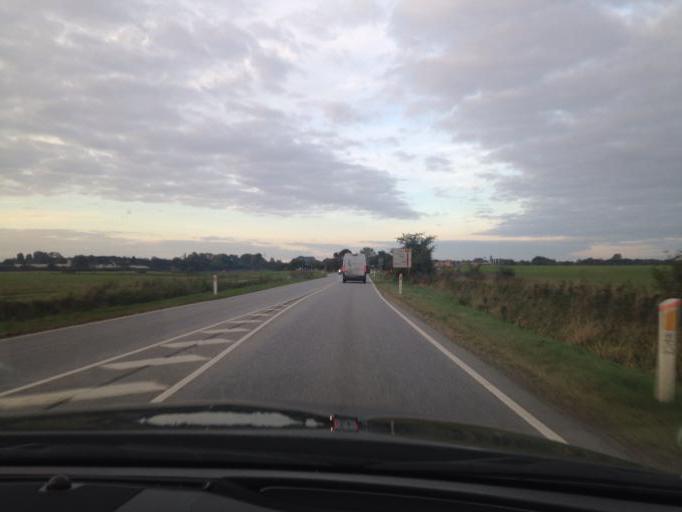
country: DK
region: South Denmark
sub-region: Haderslev Kommune
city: Vojens
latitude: 55.2549
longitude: 9.3247
